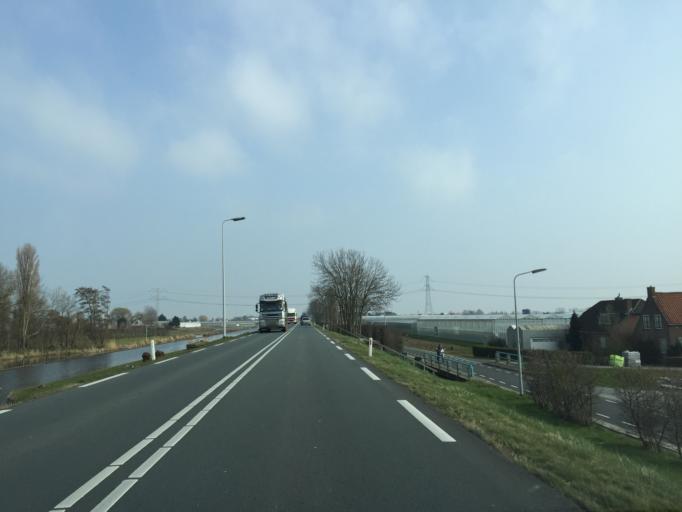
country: NL
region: South Holland
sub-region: Gemeente Westland
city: Naaldwijk
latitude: 51.9753
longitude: 4.1922
